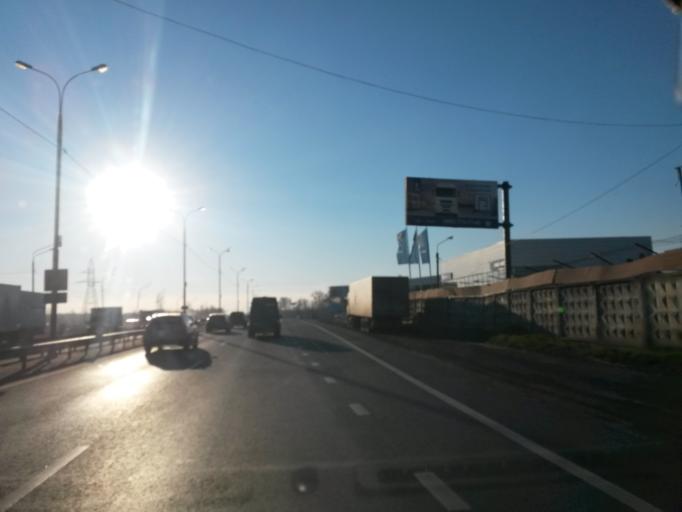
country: RU
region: Moskovskaya
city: Lesnyye Polyany
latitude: 55.9818
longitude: 37.8667
